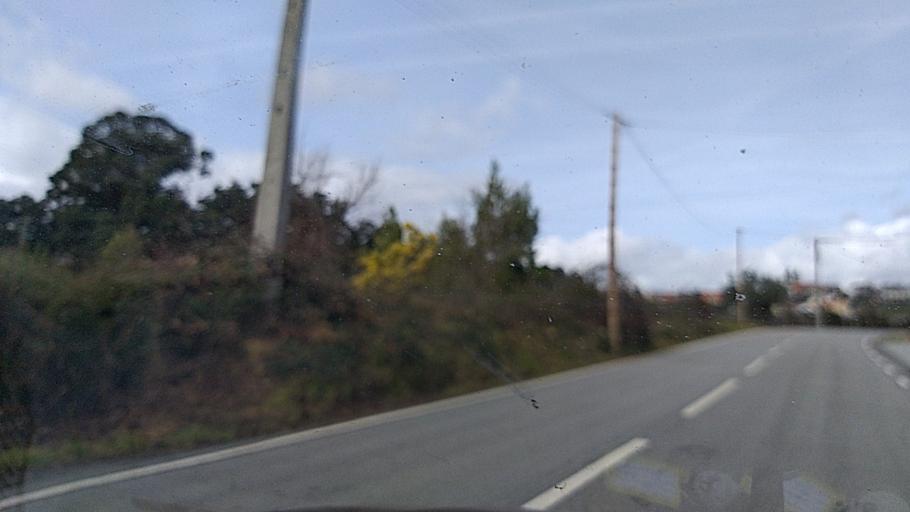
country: PT
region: Viseu
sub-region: Satao
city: Satao
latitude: 40.6700
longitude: -7.6938
